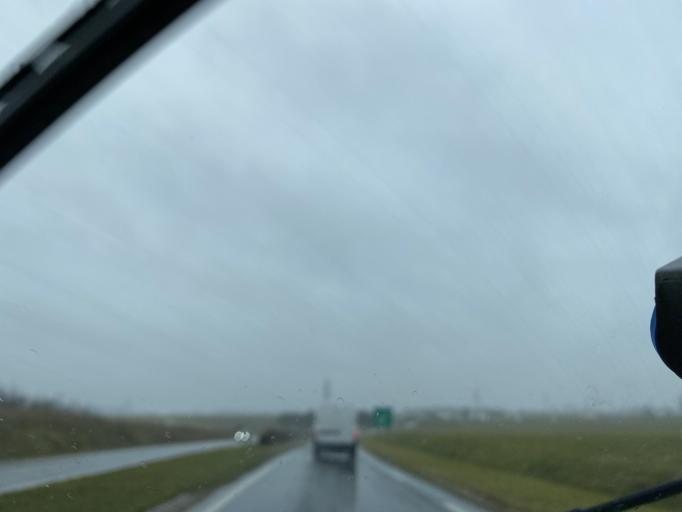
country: FR
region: Centre
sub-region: Departement d'Eure-et-Loir
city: Leves
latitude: 48.4706
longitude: 1.4645
